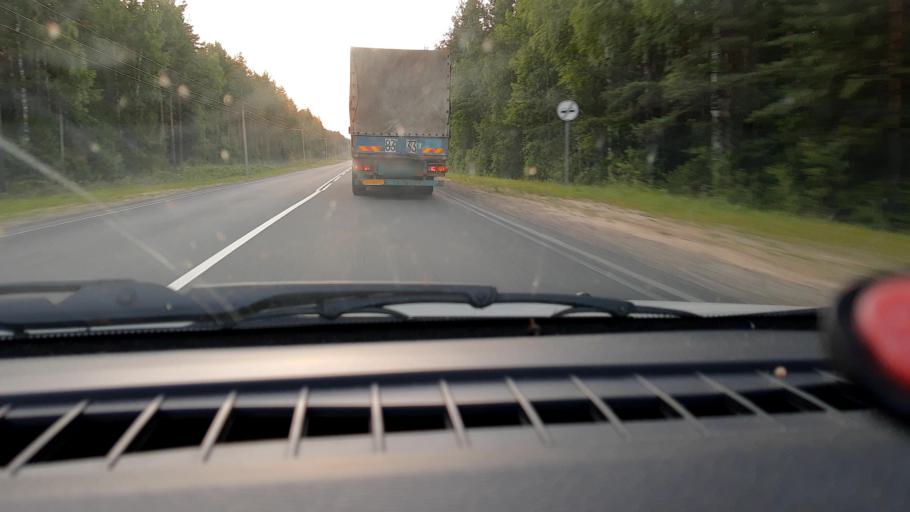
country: RU
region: Nizjnij Novgorod
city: Uren'
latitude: 57.3562
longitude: 45.7014
